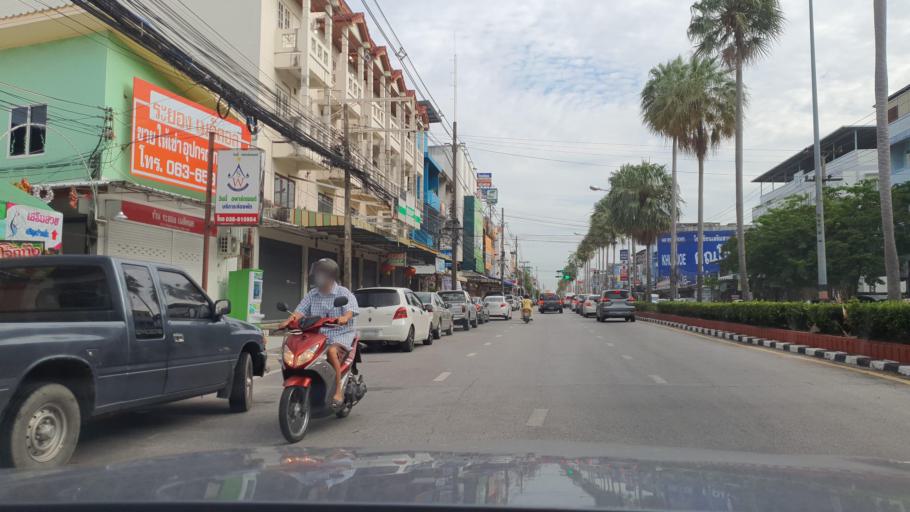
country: TH
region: Rayong
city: Rayong
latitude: 12.6836
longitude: 101.2756
